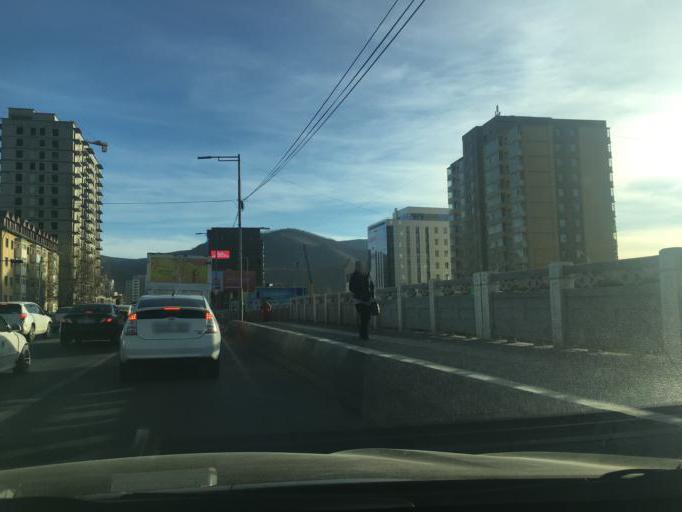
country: MN
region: Ulaanbaatar
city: Ulaanbaatar
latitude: 47.9024
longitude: 106.8930
